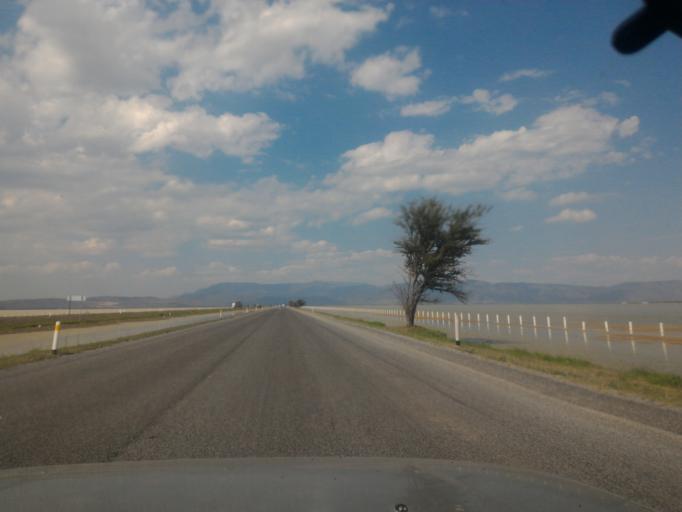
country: MX
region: Jalisco
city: Atoyac
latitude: 20.0632
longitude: -103.5217
